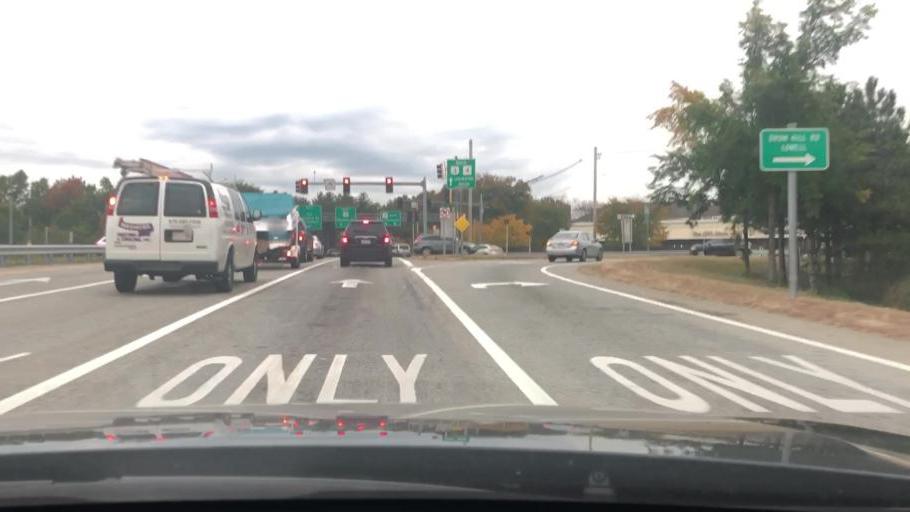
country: US
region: Massachusetts
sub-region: Middlesex County
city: Chelmsford
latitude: 42.6225
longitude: -71.3643
